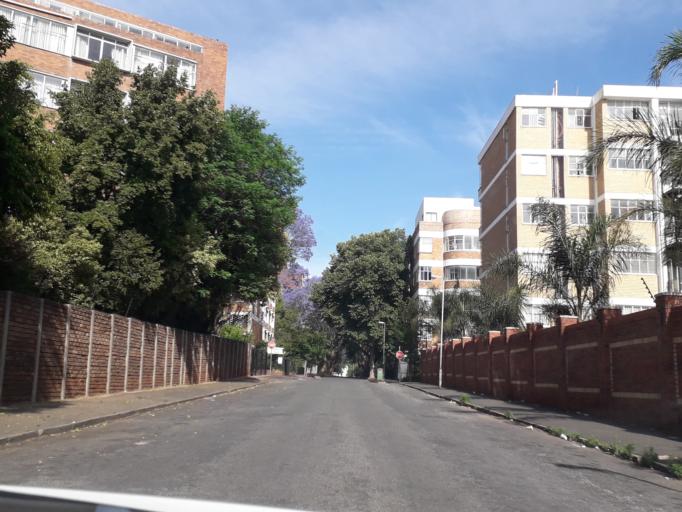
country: ZA
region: Gauteng
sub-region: City of Johannesburg Metropolitan Municipality
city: Johannesburg
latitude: -26.1666
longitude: 28.0523
